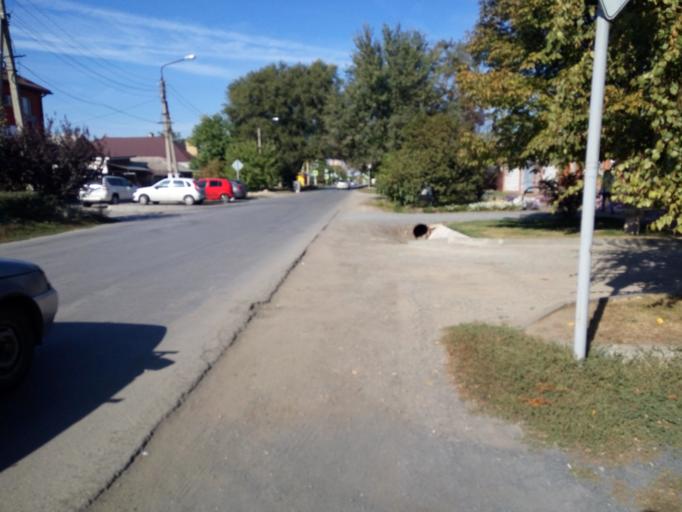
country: RU
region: Rostov
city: Bataysk
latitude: 47.1423
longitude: 39.7360
